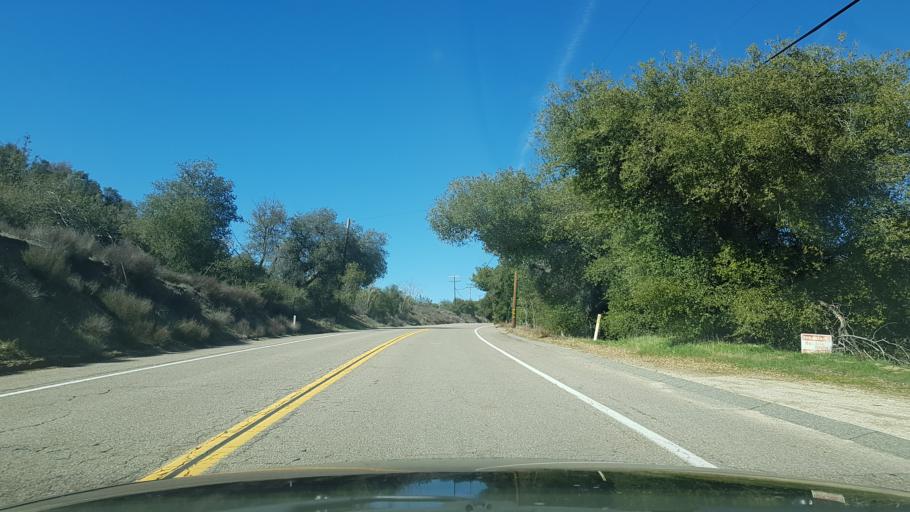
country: US
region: California
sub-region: San Diego County
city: Julian
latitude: 33.2017
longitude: -116.6018
